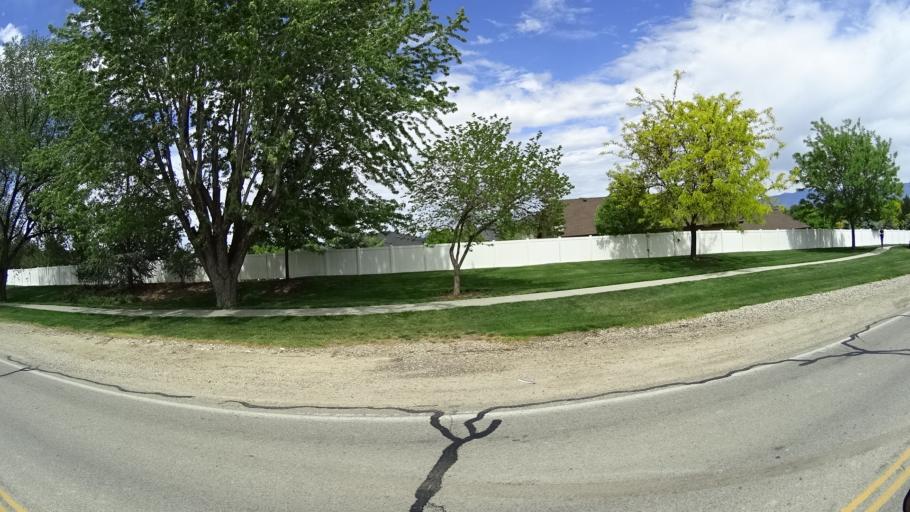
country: US
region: Idaho
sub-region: Ada County
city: Meridian
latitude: 43.5756
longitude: -116.4020
